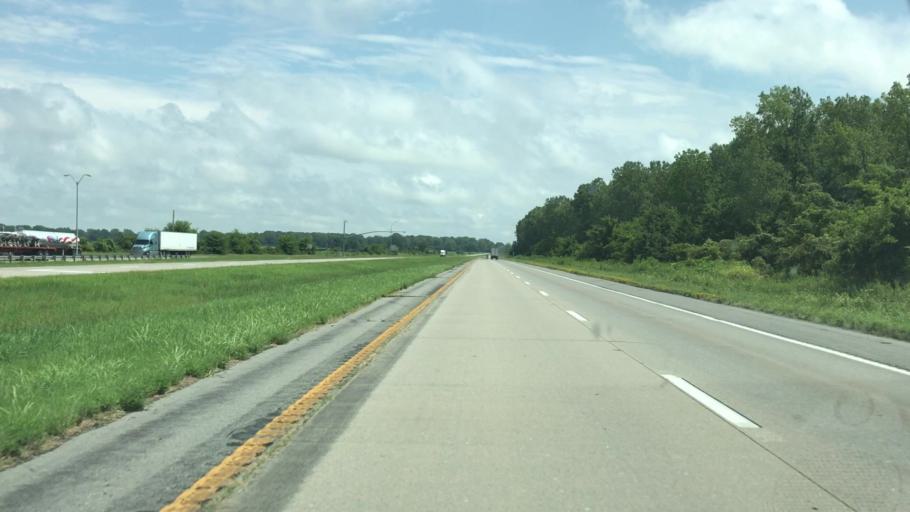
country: US
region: Missouri
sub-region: Pemiscot County
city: Caruthersville
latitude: 36.1431
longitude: -89.6444
